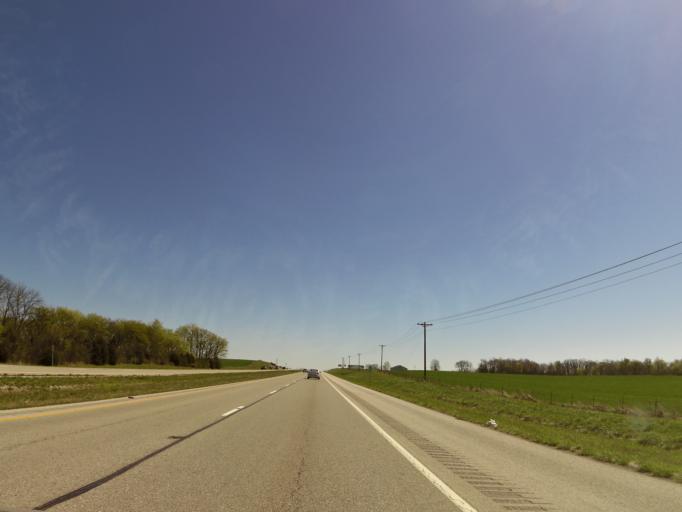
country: US
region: Kentucky
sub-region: Logan County
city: Auburn
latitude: 36.8703
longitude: -86.7030
